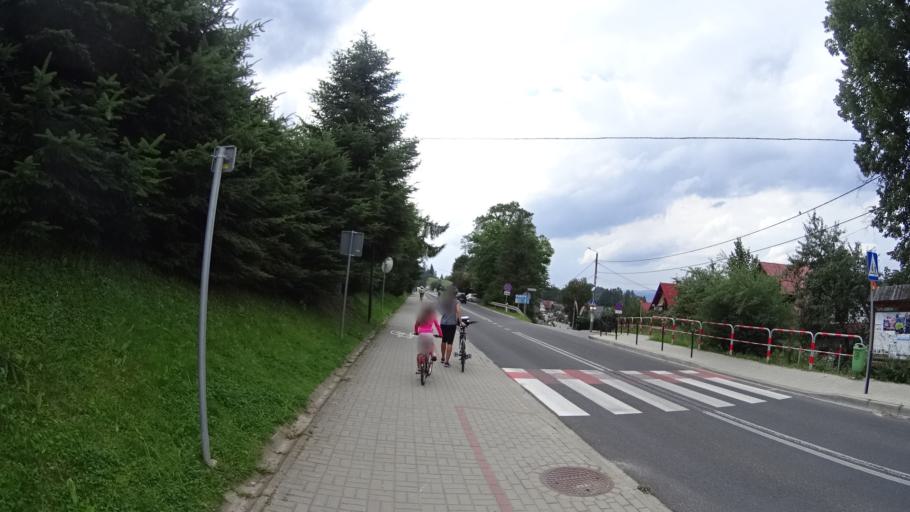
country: PL
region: Lesser Poland Voivodeship
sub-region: Powiat nowotarski
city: Niedzica
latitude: 49.4223
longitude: 20.3150
